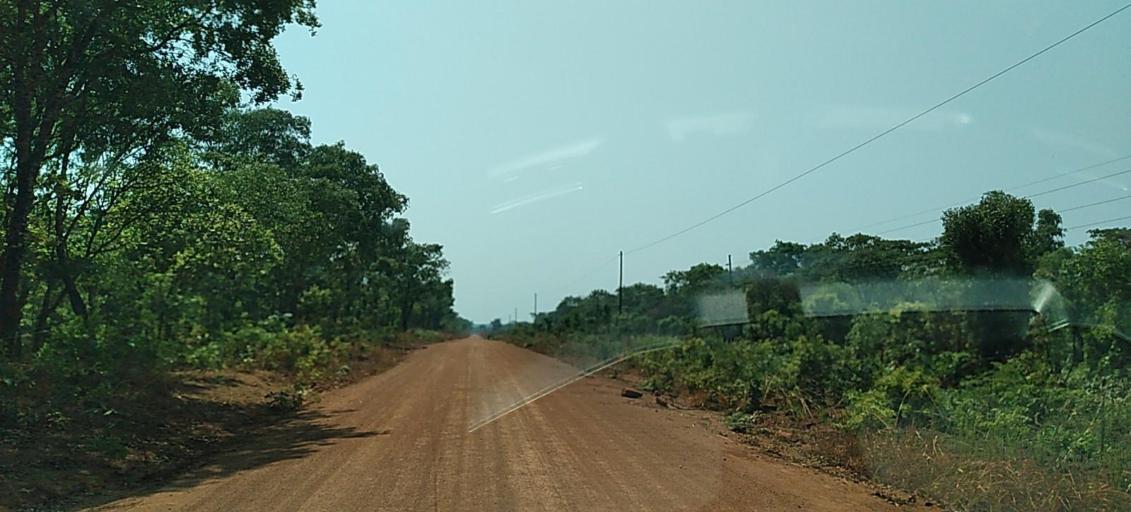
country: ZM
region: North-Western
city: Kansanshi
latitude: -11.9947
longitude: 26.6482
